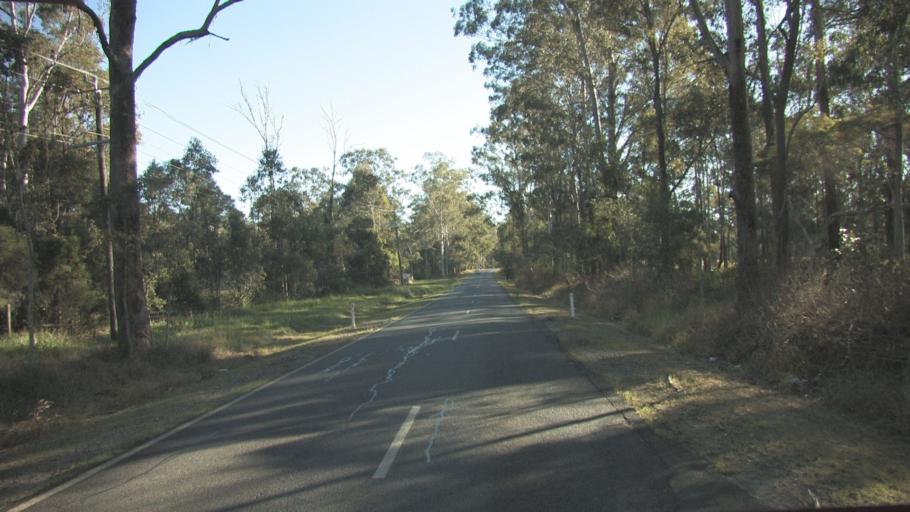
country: AU
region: Queensland
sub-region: Logan
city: Chambers Flat
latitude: -27.7801
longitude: 153.0680
